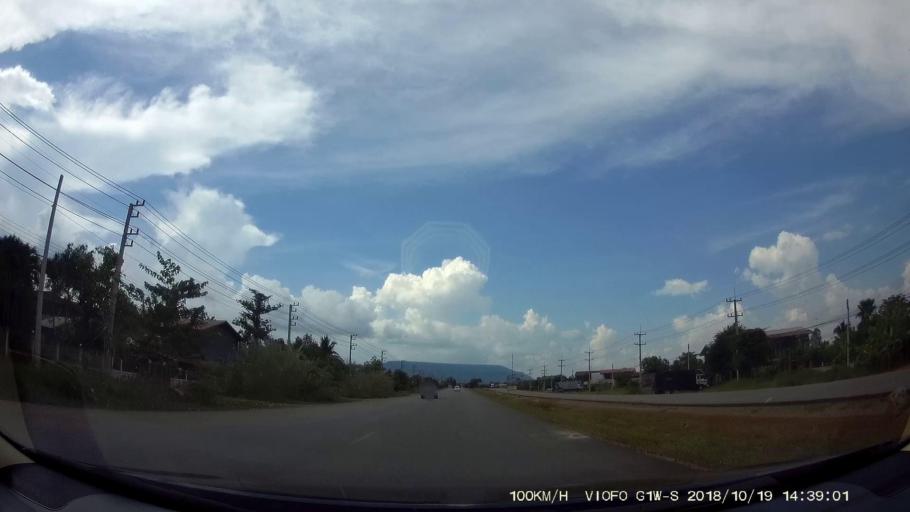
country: TH
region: Chaiyaphum
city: Kaeng Khro
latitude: 16.2215
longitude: 102.1964
